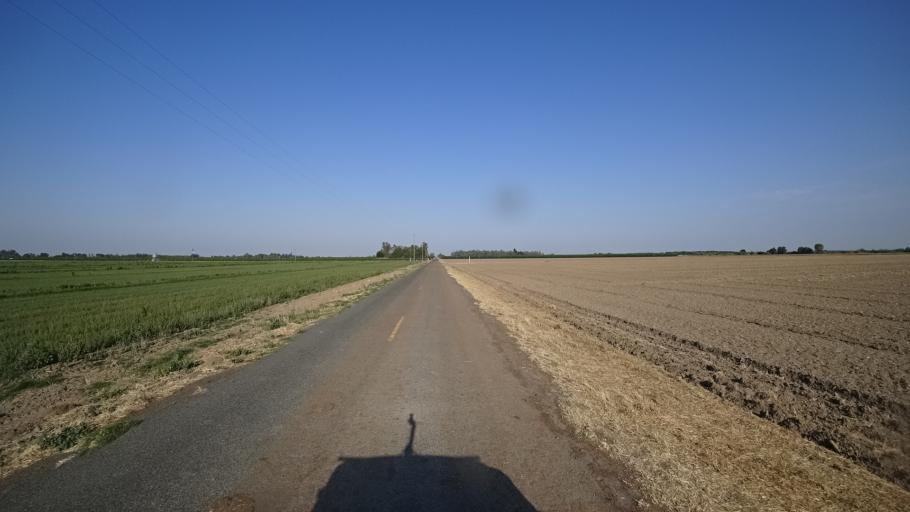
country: US
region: California
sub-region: Fresno County
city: Riverdale
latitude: 36.3803
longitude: -119.7993
